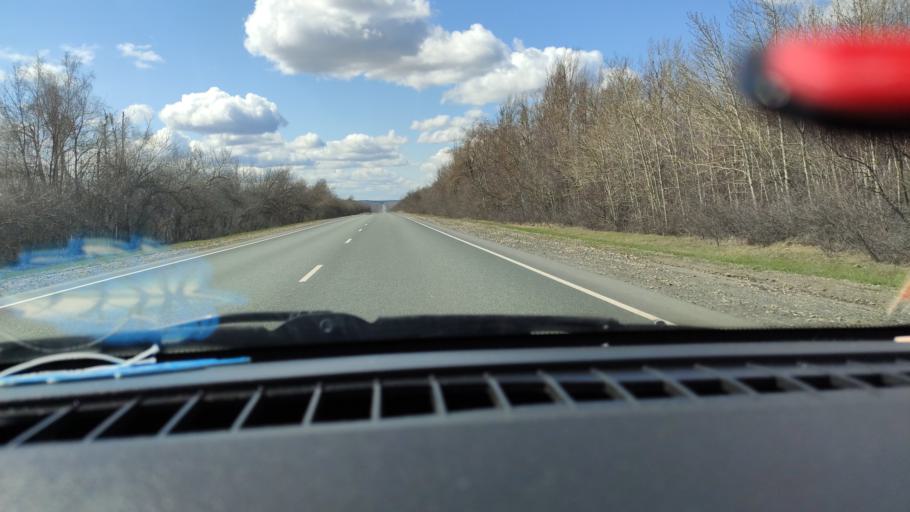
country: RU
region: Saratov
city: Khvalynsk
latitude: 52.5949
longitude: 48.1363
